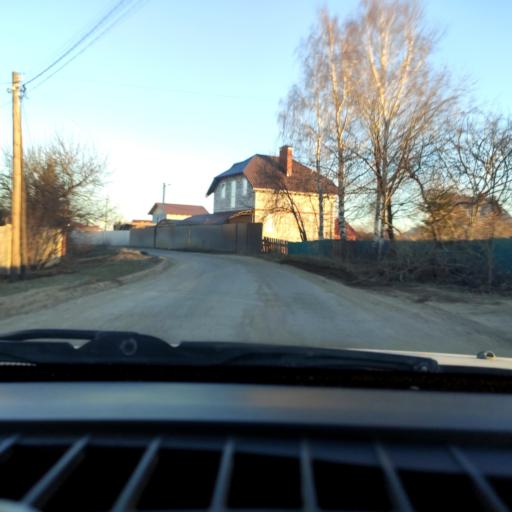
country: RU
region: Perm
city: Kultayevo
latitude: 57.9342
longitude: 56.0135
